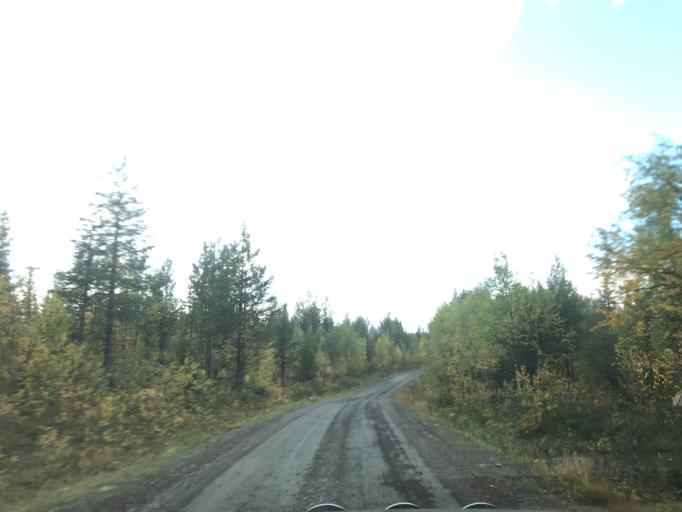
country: SE
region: Norrbotten
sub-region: Gallivare Kommun
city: Malmberget
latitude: 67.5857
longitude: 20.8703
